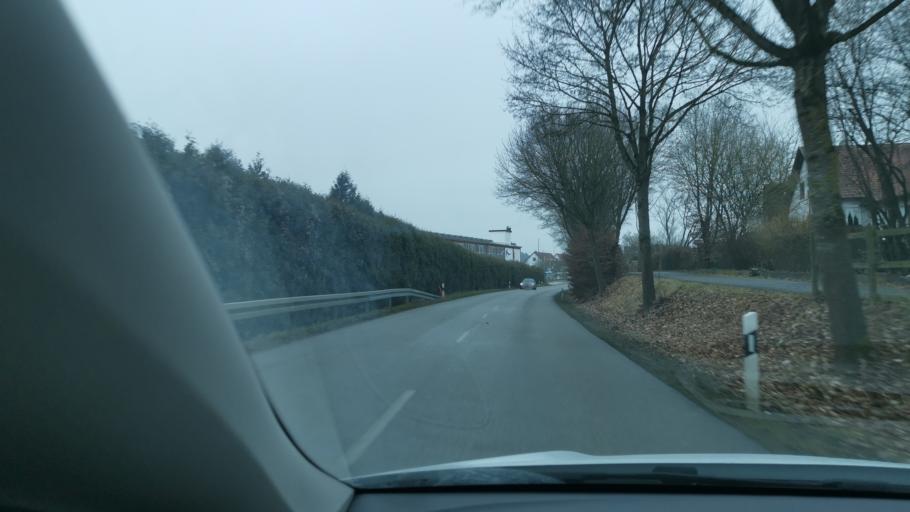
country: DE
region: Bavaria
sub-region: Swabia
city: Holzheim
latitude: 48.5901
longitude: 10.9593
